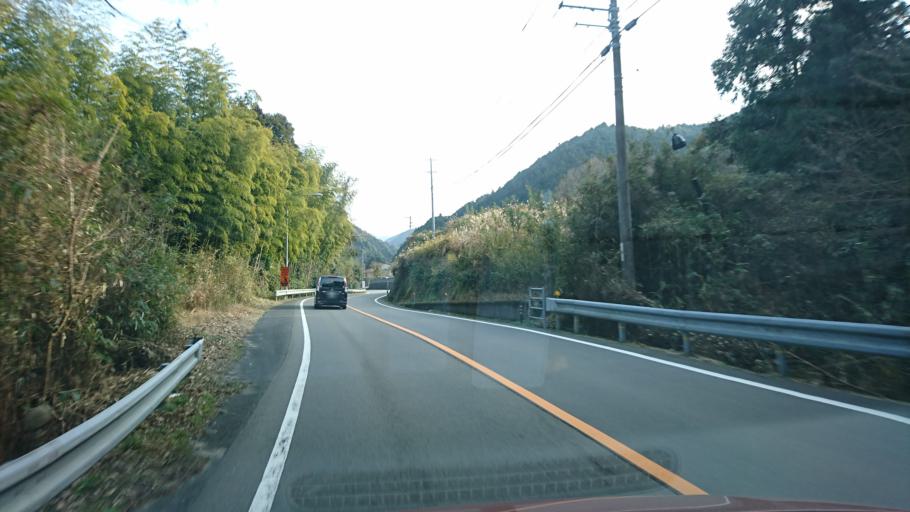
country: JP
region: Ehime
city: Hojo
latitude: 33.9703
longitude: 132.9024
